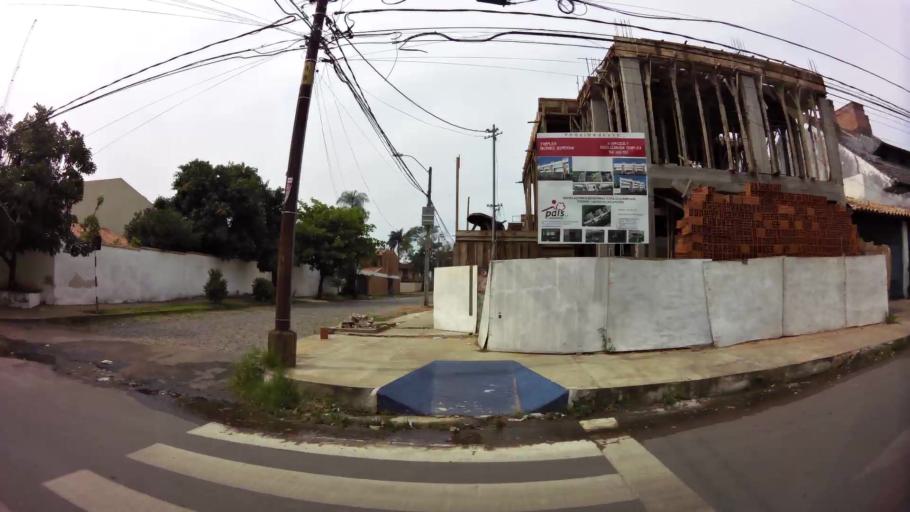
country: PY
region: Central
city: Lambare
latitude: -25.2935
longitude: -57.5719
